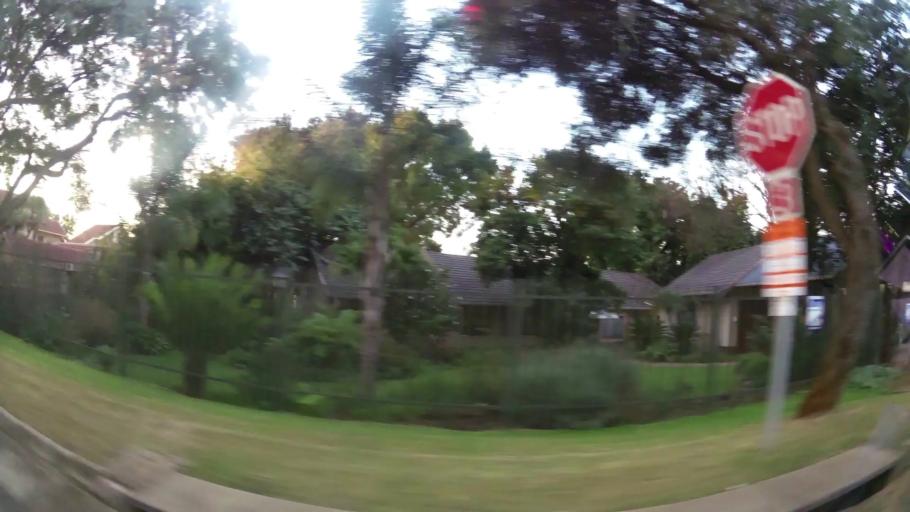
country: ZA
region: Gauteng
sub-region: City of Tshwane Metropolitan Municipality
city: Centurion
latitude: -25.8378
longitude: 28.1523
